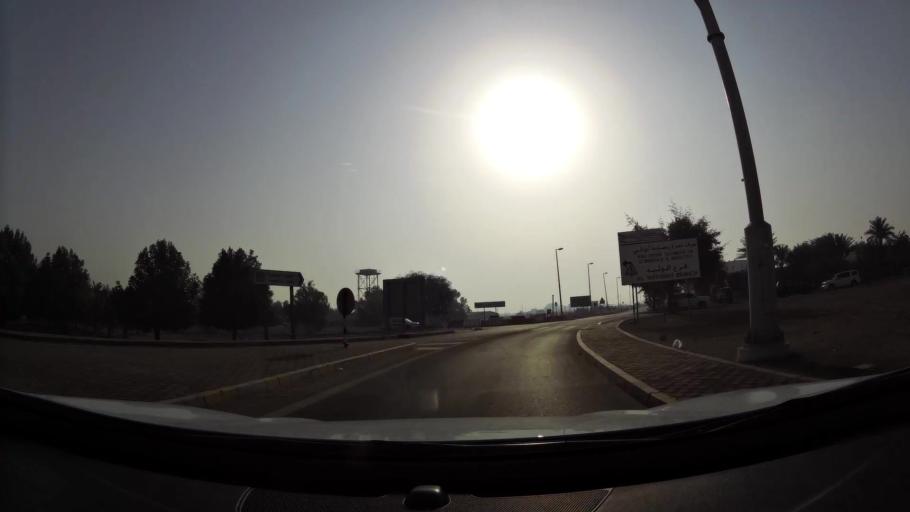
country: AE
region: Abu Dhabi
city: Abu Dhabi
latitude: 24.2781
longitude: 54.6459
